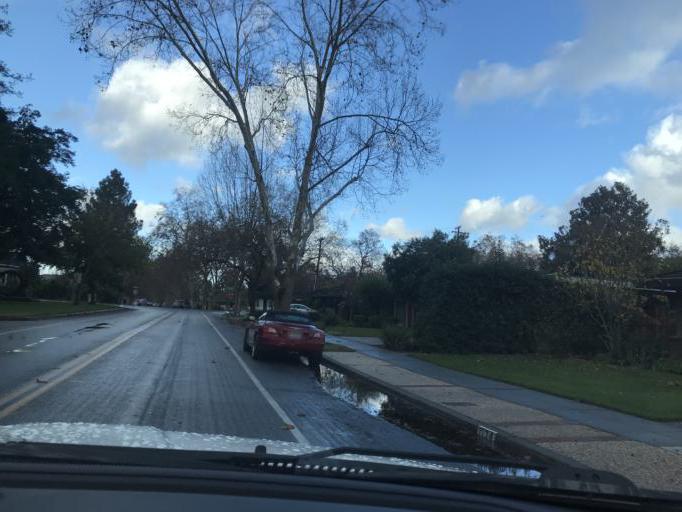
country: US
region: California
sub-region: Santa Clara County
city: Buena Vista
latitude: 37.3045
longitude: -121.9077
